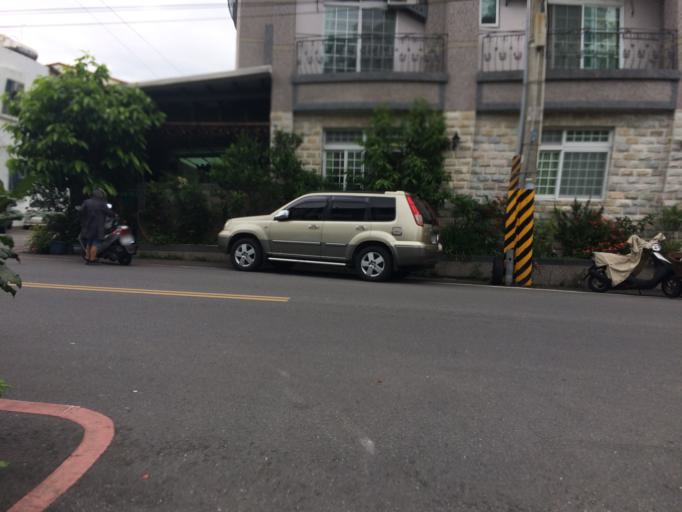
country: TW
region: Taiwan
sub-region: Hualien
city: Hualian
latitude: 23.9701
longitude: 121.6017
